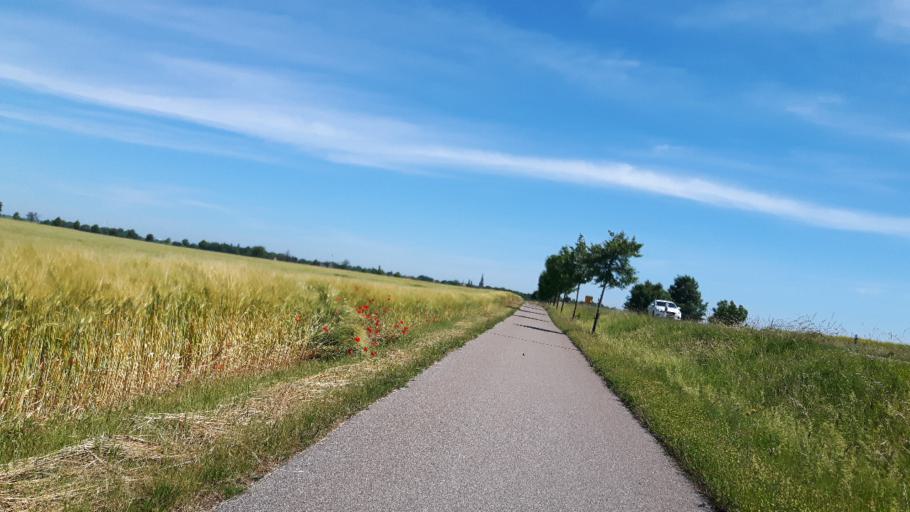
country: DE
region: Saxony-Anhalt
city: Lutzen
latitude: 51.2429
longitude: 12.1215
